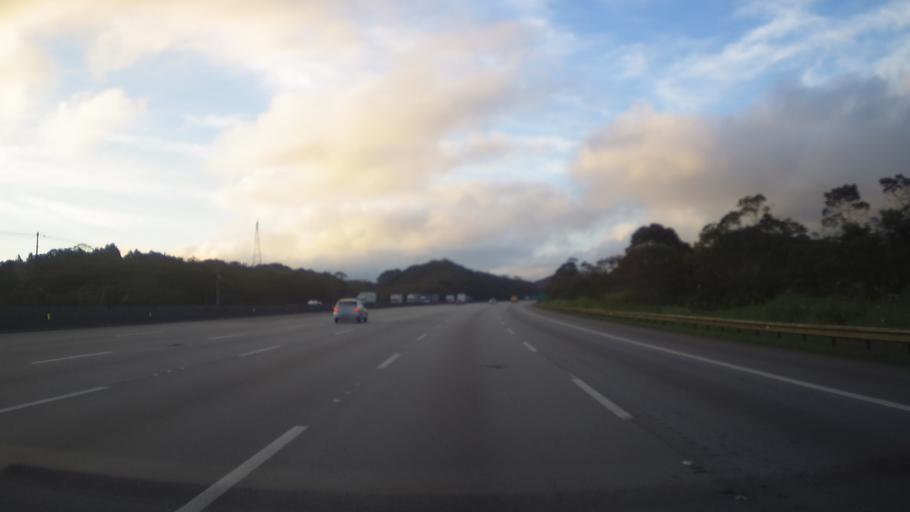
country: BR
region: Sao Paulo
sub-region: Cubatao
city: Cubatao
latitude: -23.8671
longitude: -46.5726
